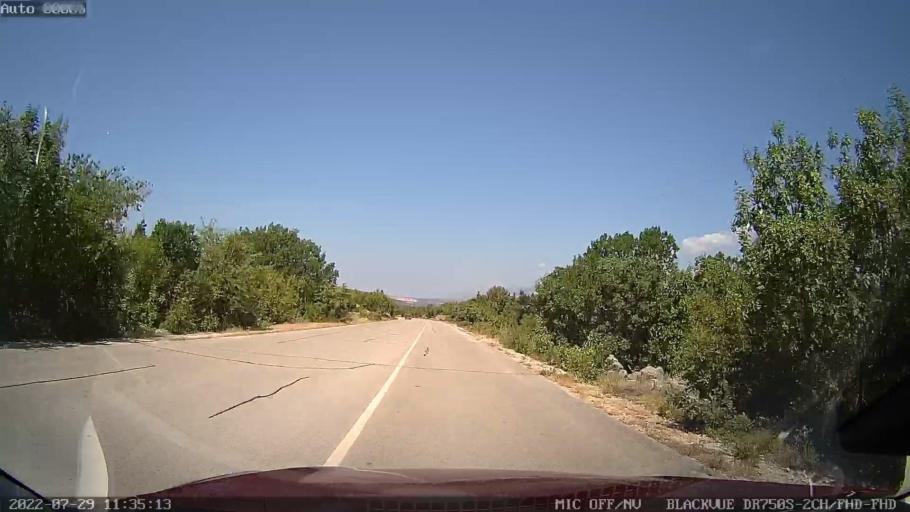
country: HR
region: Zadarska
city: Obrovac
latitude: 44.1814
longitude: 15.7158
